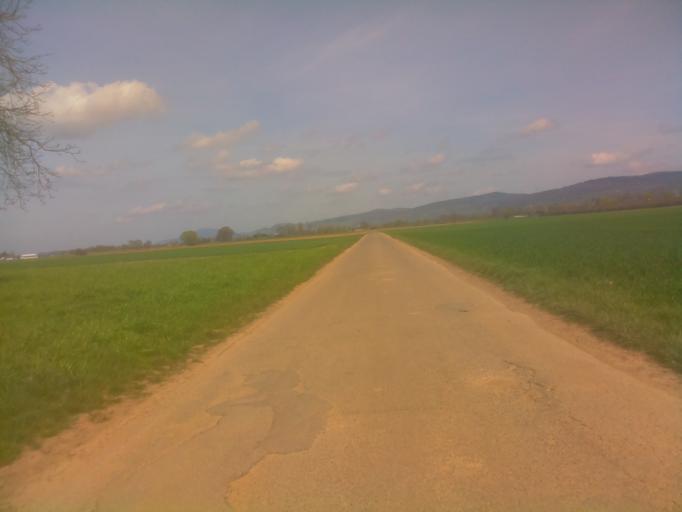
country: DE
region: Baden-Wuerttemberg
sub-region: Karlsruhe Region
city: Hemsbach
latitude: 49.5642
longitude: 8.6274
